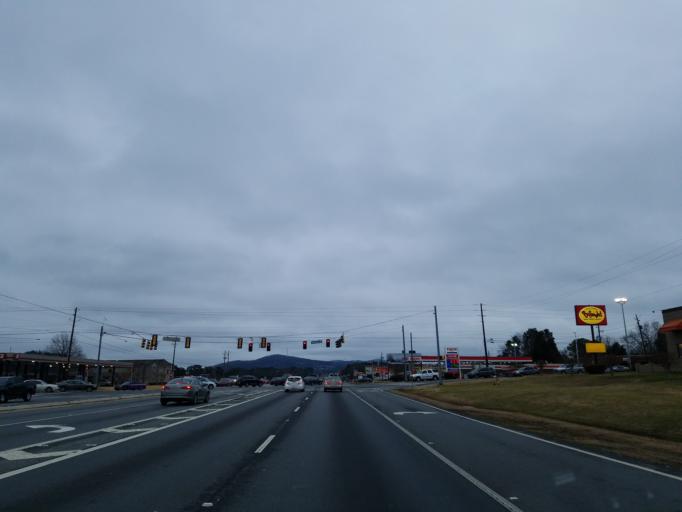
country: US
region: Georgia
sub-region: Bartow County
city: Cartersville
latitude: 34.2072
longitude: -84.8202
